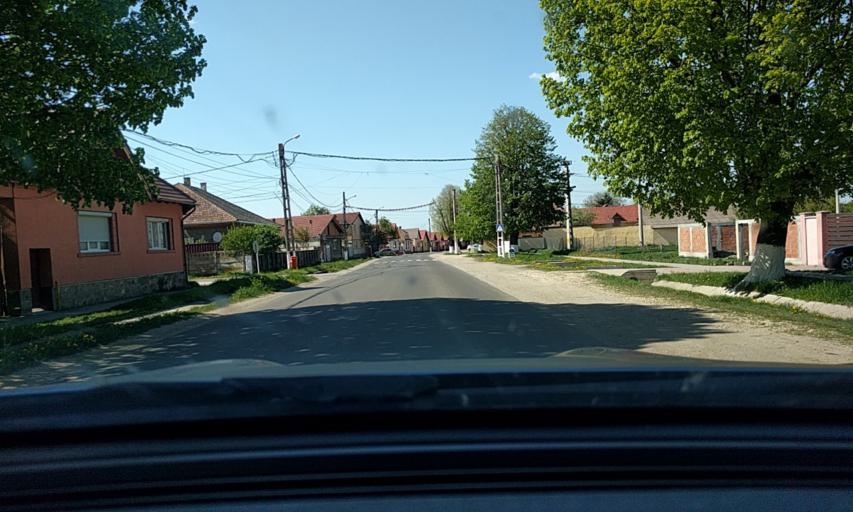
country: RO
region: Brasov
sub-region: Comuna Harman
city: Harman
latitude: 45.7088
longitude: 25.6860
